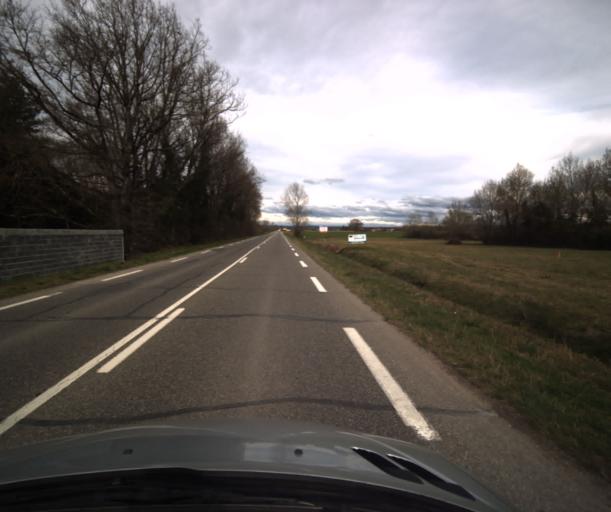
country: FR
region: Midi-Pyrenees
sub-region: Departement du Tarn-et-Garonne
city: Negrepelisse
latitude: 44.0633
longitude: 1.4961
